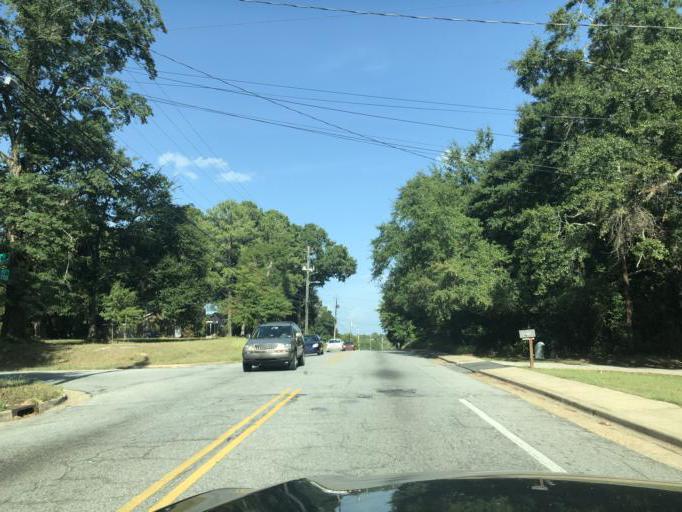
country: US
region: Georgia
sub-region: Muscogee County
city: Columbus
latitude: 32.4842
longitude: -84.9298
